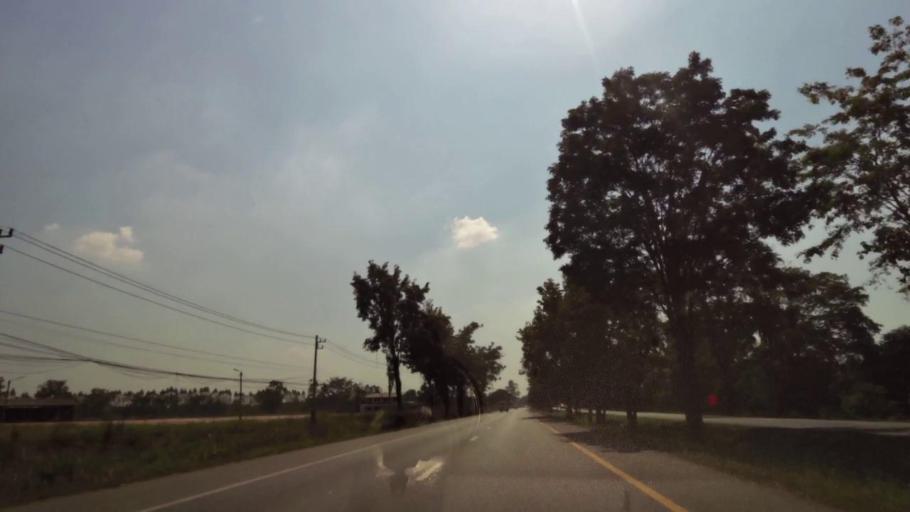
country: TH
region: Phichit
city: Bueng Na Rang
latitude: 16.1774
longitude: 100.1281
